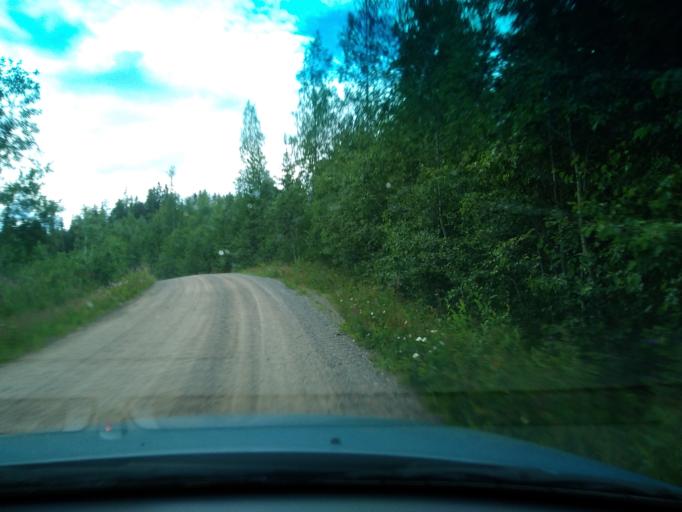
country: FI
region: Central Finland
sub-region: Saarijaervi-Viitasaari
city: Karstula
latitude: 62.7865
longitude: 24.9438
